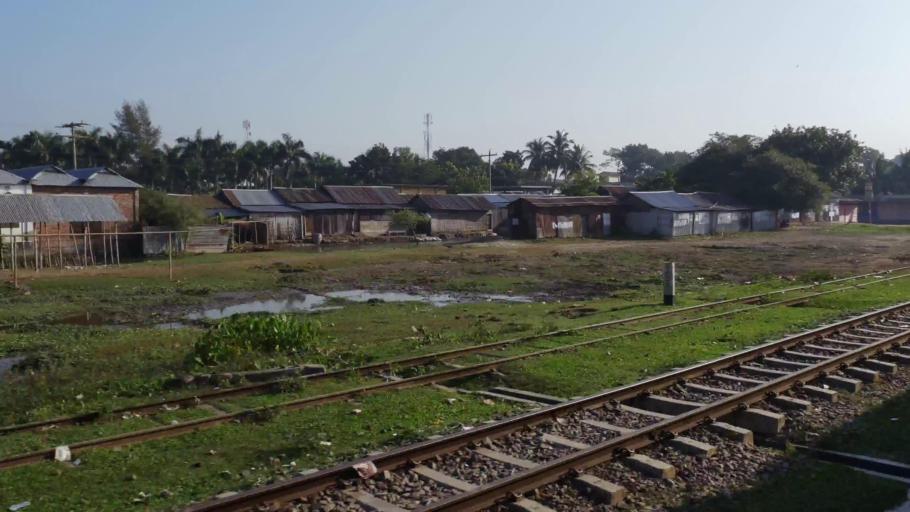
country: BD
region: Dhaka
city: Jamalpur
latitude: 24.8638
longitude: 90.1061
